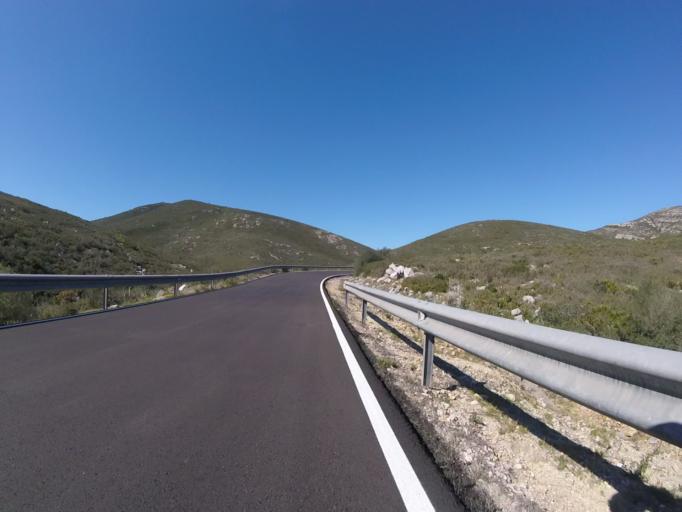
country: ES
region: Valencia
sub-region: Provincia de Castello
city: Cervera del Maestre
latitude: 40.4029
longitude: 0.2285
